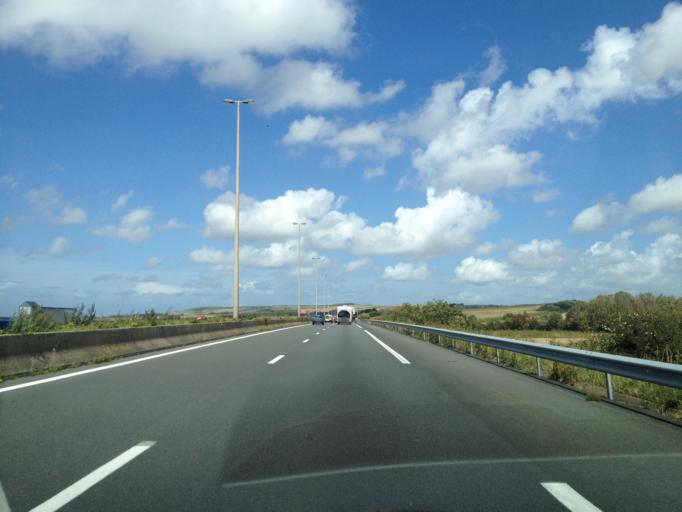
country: FR
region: Nord-Pas-de-Calais
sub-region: Departement du Pas-de-Calais
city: Marquise
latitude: 50.8207
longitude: 1.6975
